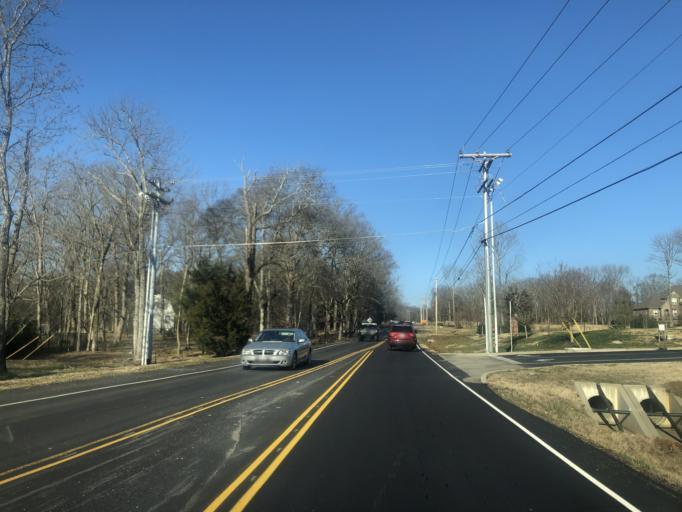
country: US
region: Tennessee
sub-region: Williamson County
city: Nolensville
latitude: 35.9641
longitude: -86.6922
